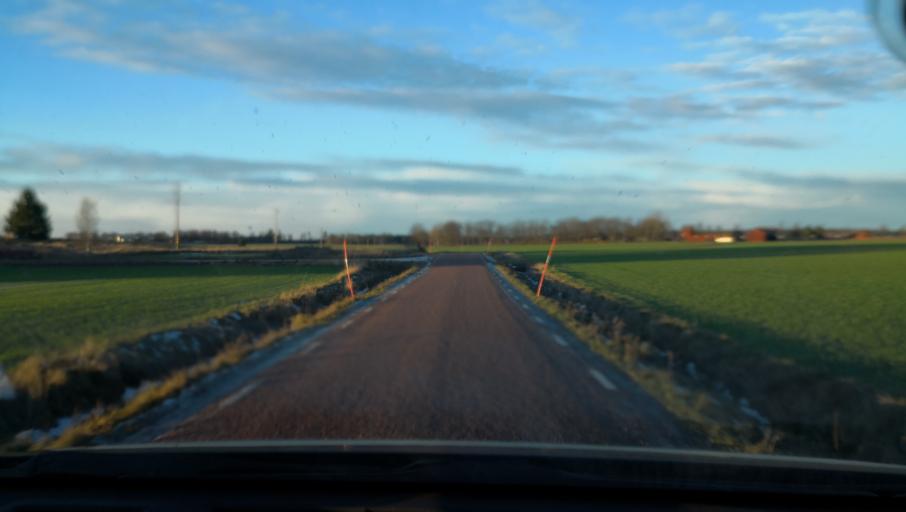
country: SE
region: Vaestmanland
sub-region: Vasteras
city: Tillberga
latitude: 59.6938
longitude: 16.6011
